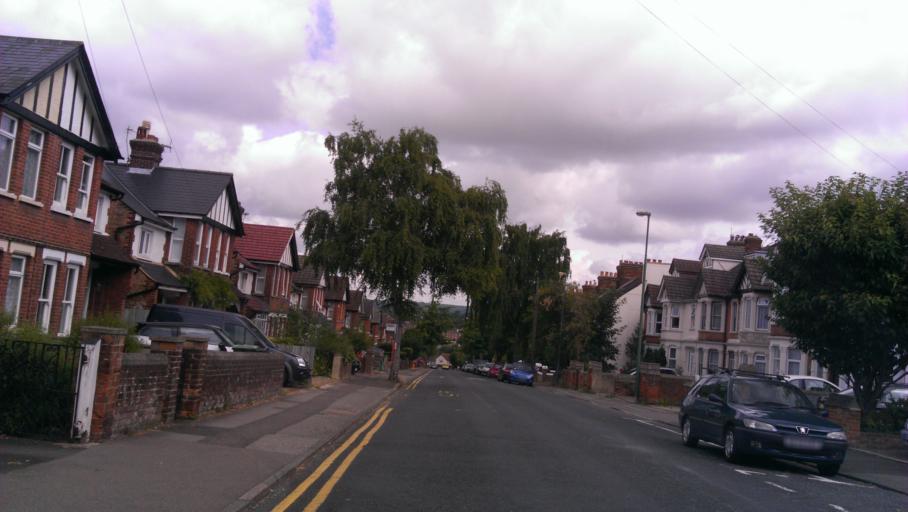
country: GB
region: England
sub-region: Kent
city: Maidstone
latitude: 51.2674
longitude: 0.5296
